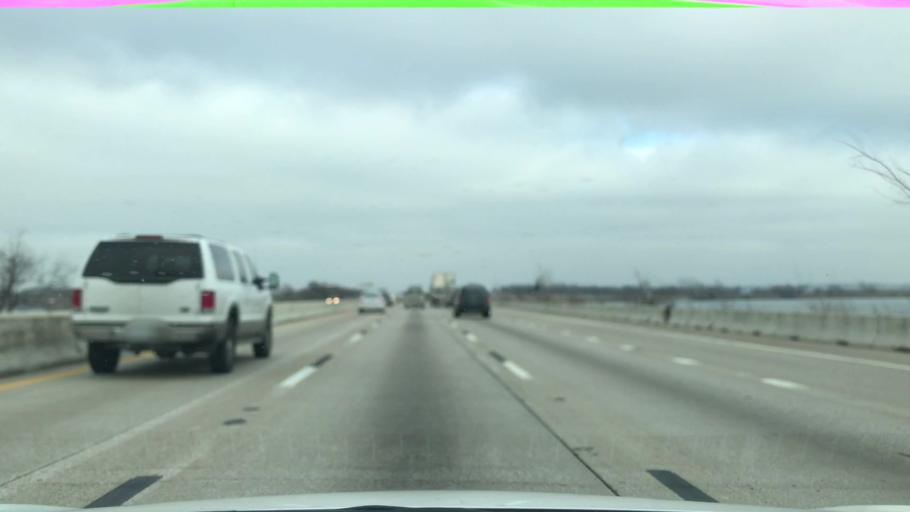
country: US
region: Texas
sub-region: Dallas County
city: Rowlett
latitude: 32.8716
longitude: -96.5290
